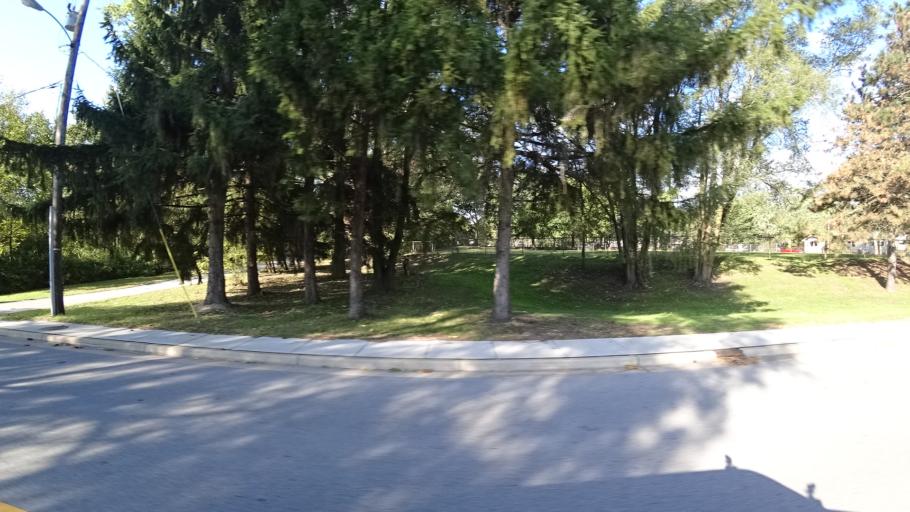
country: US
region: Indiana
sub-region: LaPorte County
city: Trail Creek
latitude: 41.7089
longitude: -86.8648
